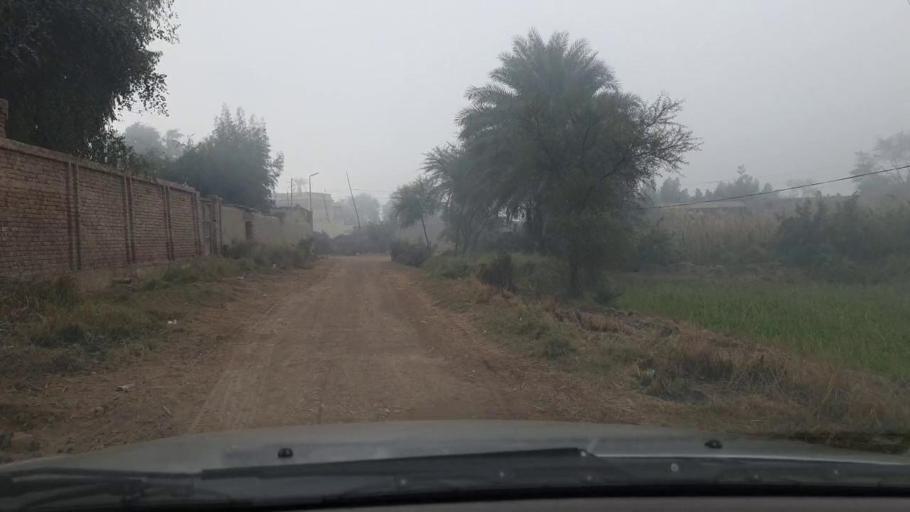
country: PK
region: Sindh
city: Khanpur
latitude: 27.8482
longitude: 69.4873
